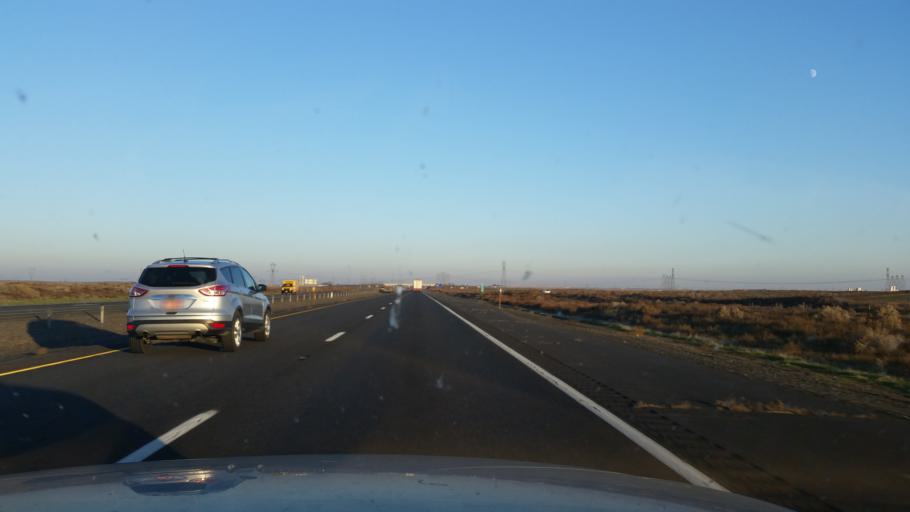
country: US
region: Washington
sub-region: Grant County
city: Royal City
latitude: 47.1042
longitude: -119.5715
